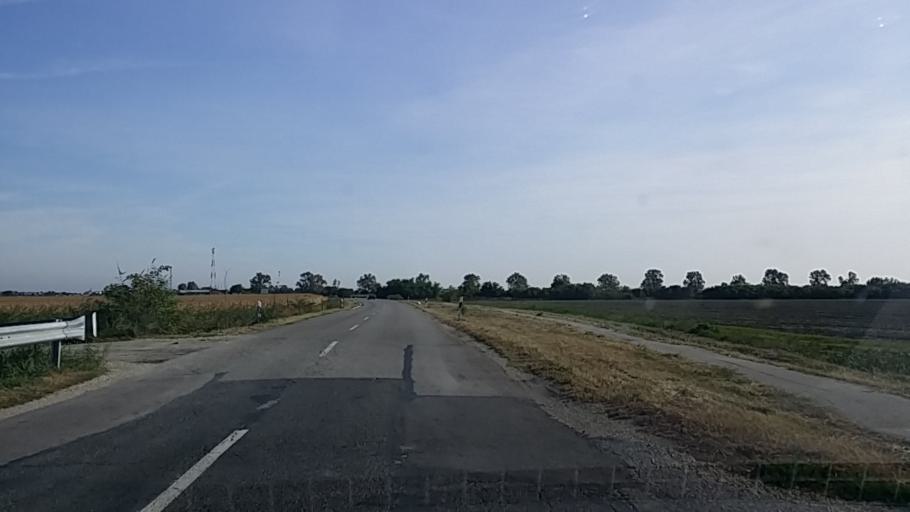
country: AT
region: Burgenland
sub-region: Politischer Bezirk Neusiedl am See
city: Pamhagen
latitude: 47.6782
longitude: 16.9102
